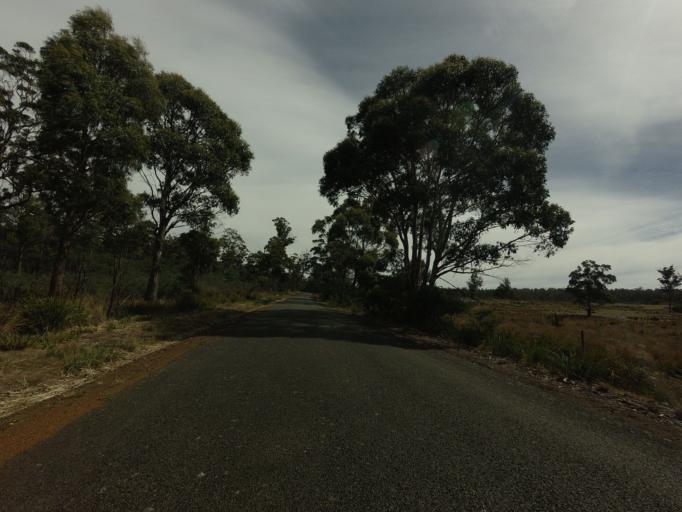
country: AU
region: Tasmania
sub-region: Sorell
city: Sorell
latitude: -42.5462
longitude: 147.6650
